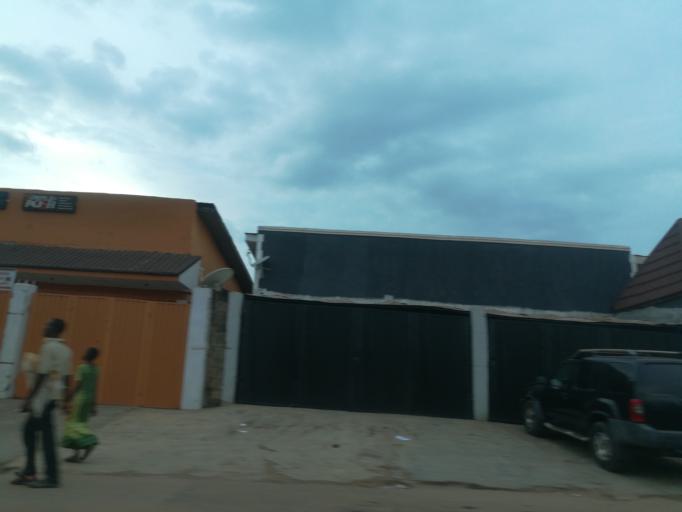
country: NG
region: Oyo
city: Ibadan
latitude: 7.4371
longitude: 3.9094
